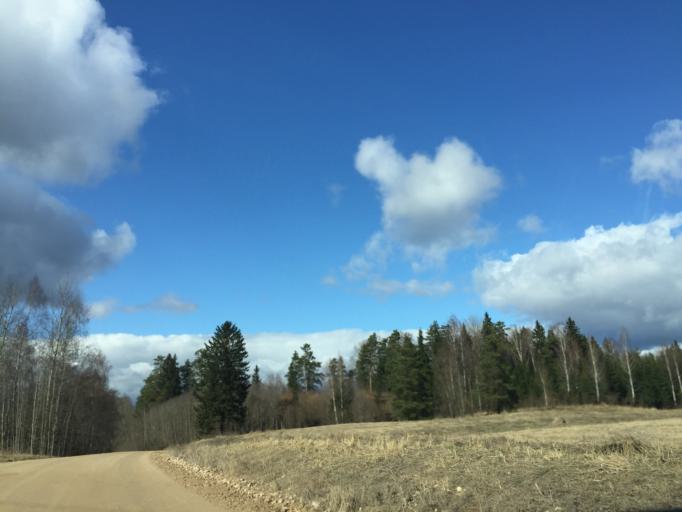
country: LV
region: Akniste
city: Akniste
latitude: 56.1215
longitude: 25.8376
